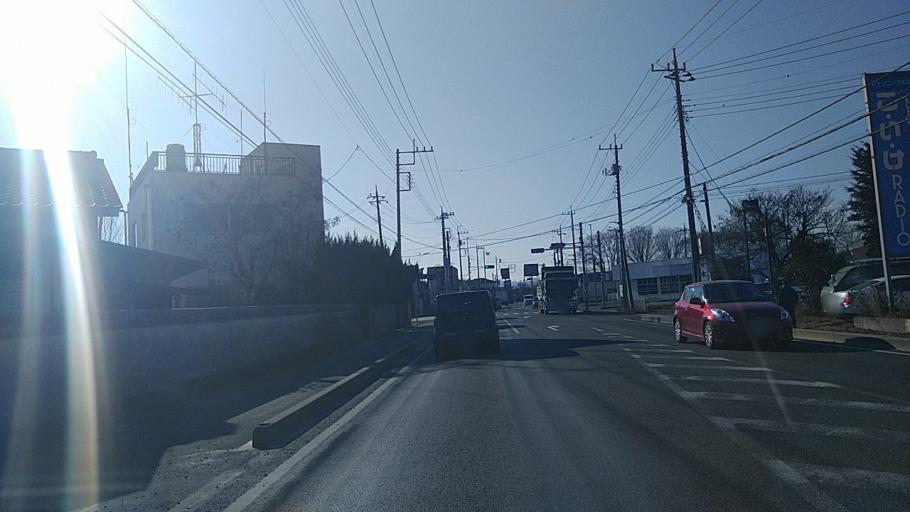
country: JP
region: Tochigi
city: Tanuma
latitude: 36.3717
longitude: 139.5846
